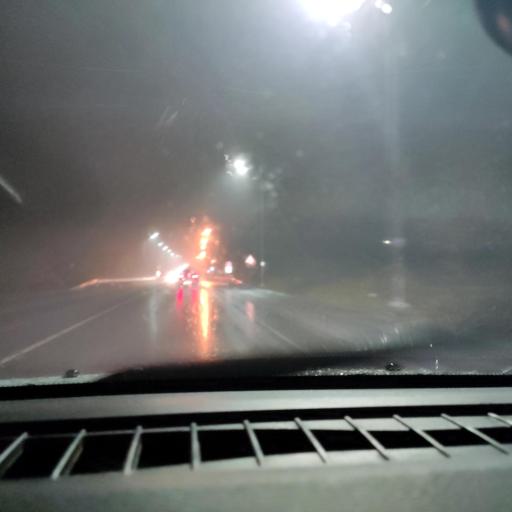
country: RU
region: Voronezj
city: Semiluki
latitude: 51.6420
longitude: 39.0154
